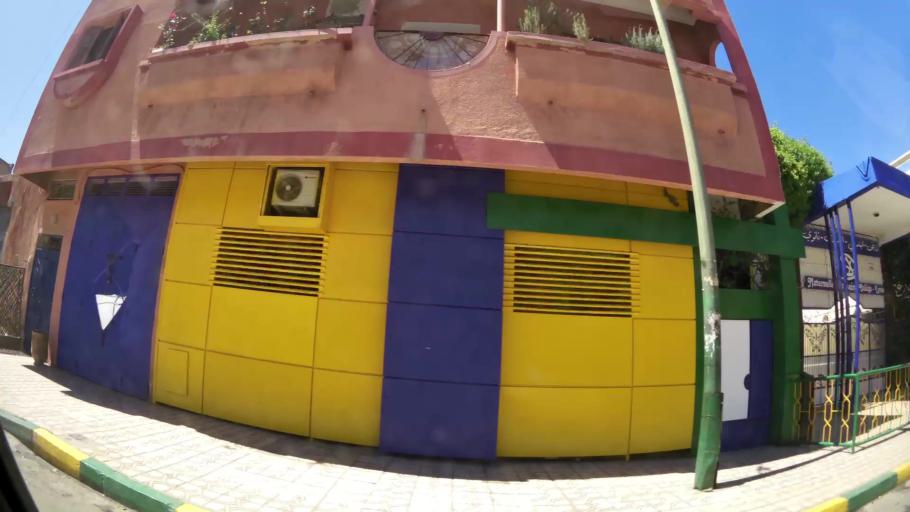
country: MA
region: Marrakech-Tensift-Al Haouz
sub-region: Marrakech
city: Marrakesh
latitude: 31.6494
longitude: -7.9945
